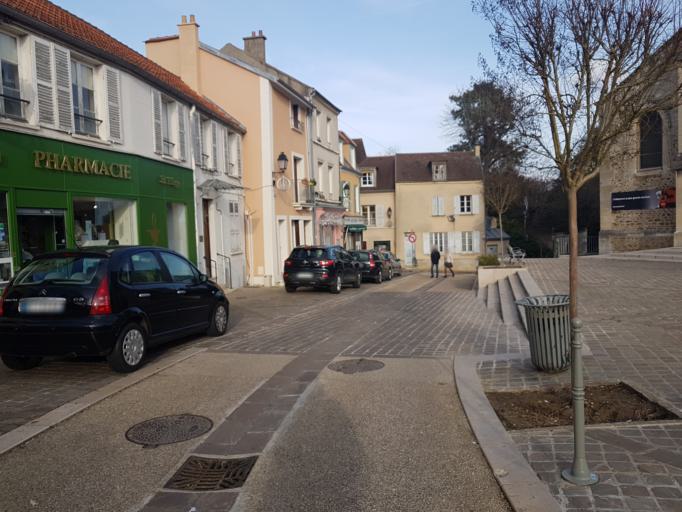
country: FR
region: Ile-de-France
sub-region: Departement des Yvelines
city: Louveciennes
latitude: 48.8610
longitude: 2.1137
